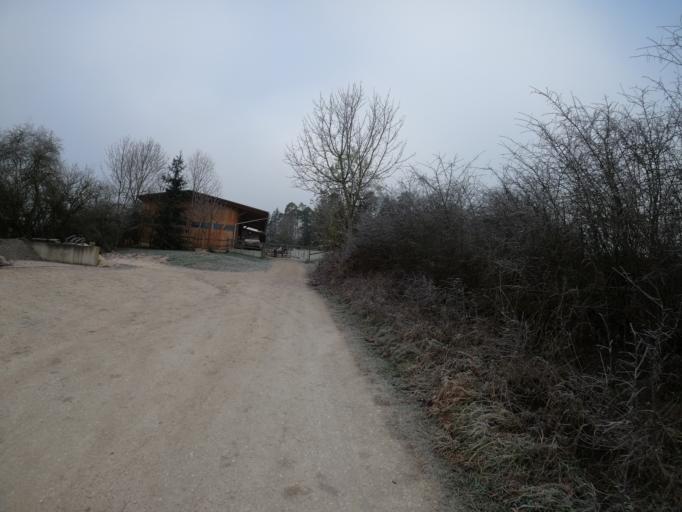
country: DE
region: Baden-Wuerttemberg
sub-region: Tuebingen Region
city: Westerstetten
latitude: 48.5149
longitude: 9.9530
